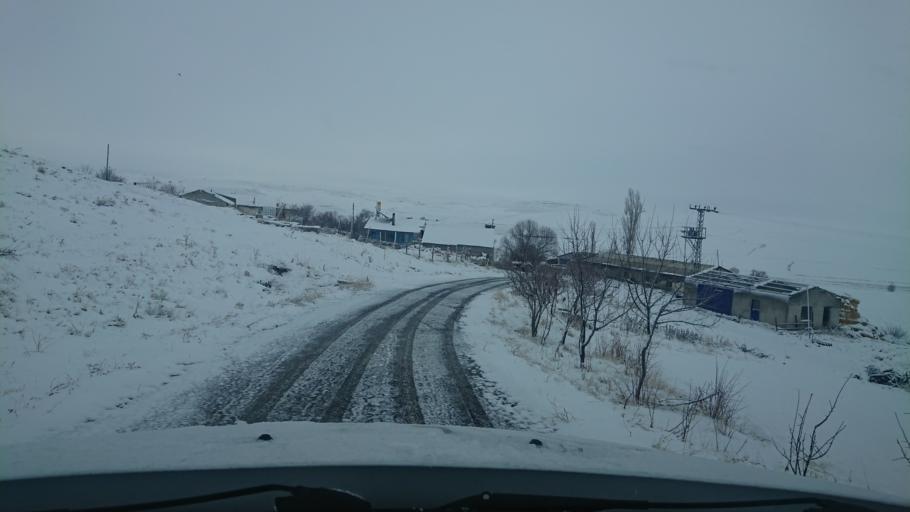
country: TR
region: Aksaray
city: Acipinar
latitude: 38.6749
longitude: 33.8656
